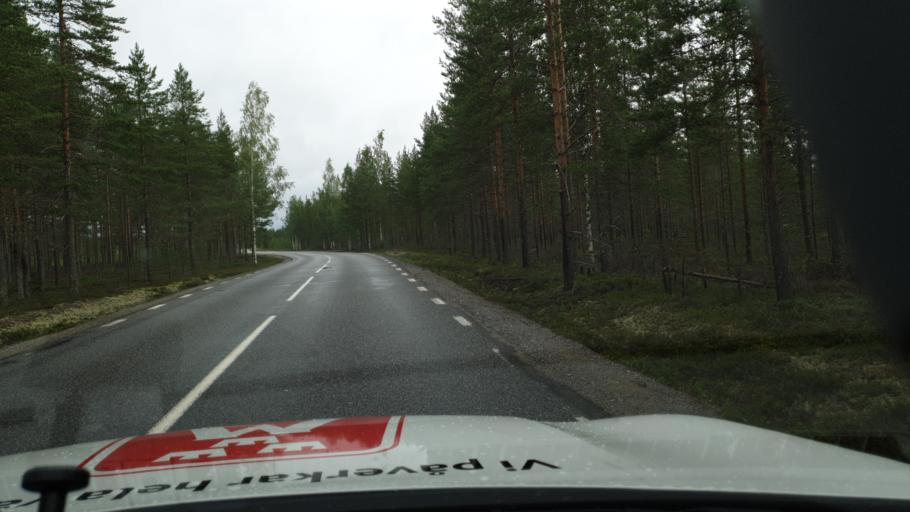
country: SE
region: Vaesterbotten
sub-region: Umea Kommun
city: Saevar
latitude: 63.9761
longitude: 20.5054
